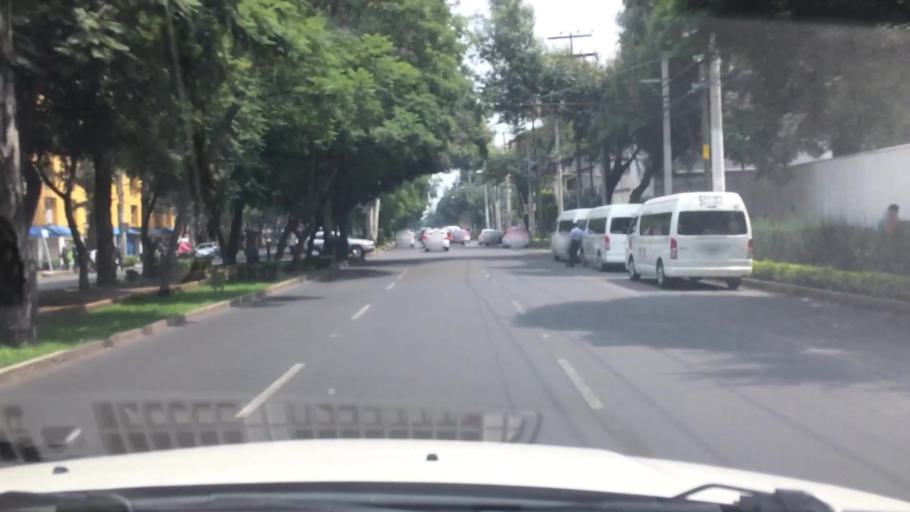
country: MX
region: Mexico City
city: Coyoacan
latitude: 19.3464
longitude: -99.1784
